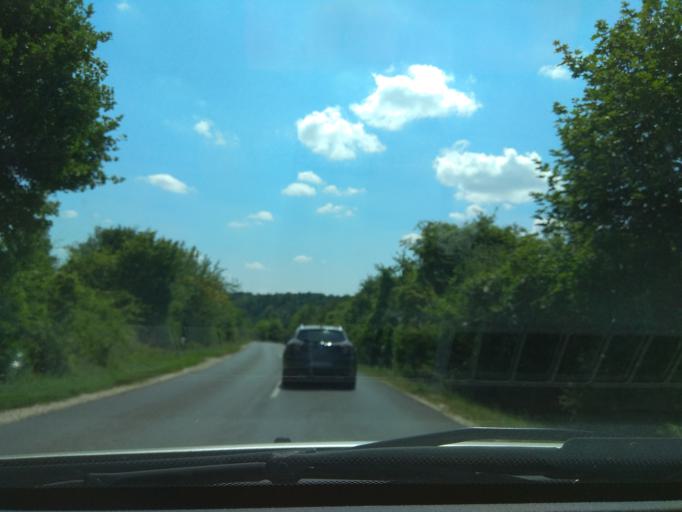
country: HU
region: Borsod-Abauj-Zemplen
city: Harsany
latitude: 48.0280
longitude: 20.7669
